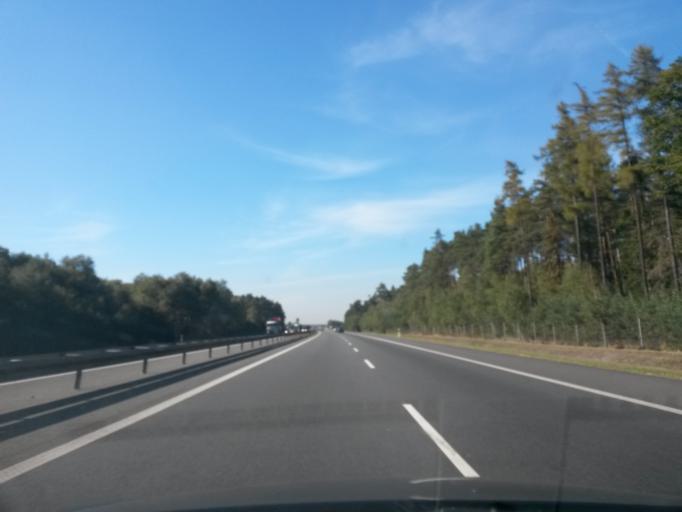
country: PL
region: Opole Voivodeship
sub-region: Powiat opolski
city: Proszkow
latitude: 50.5555
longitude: 17.8841
